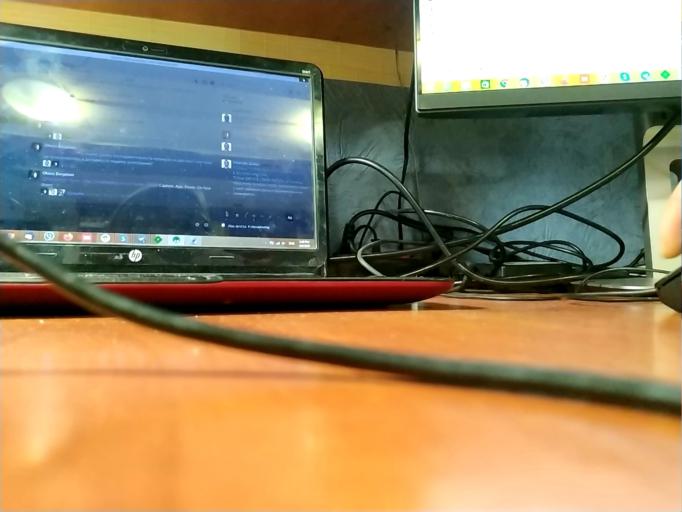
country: RU
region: Tverskaya
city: Sandovo
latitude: 58.5851
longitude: 36.4159
